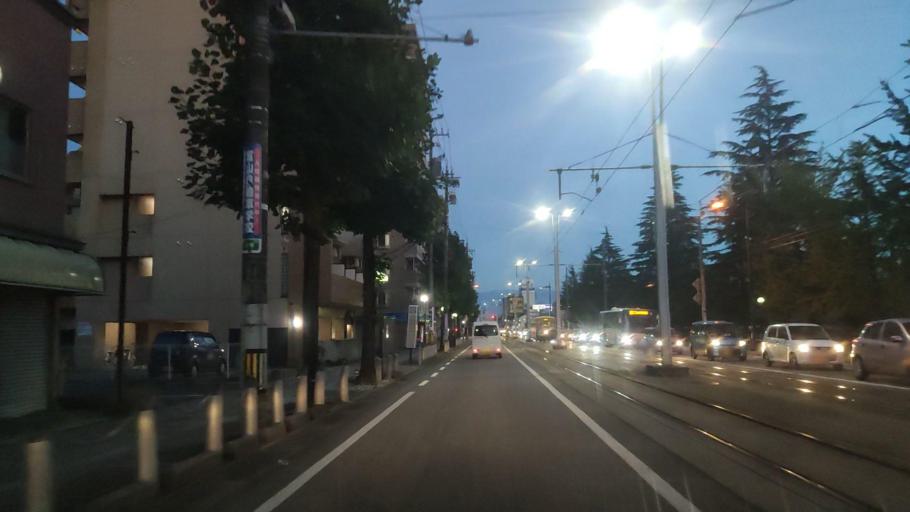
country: JP
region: Toyama
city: Toyama-shi
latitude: 36.6982
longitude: 137.1916
